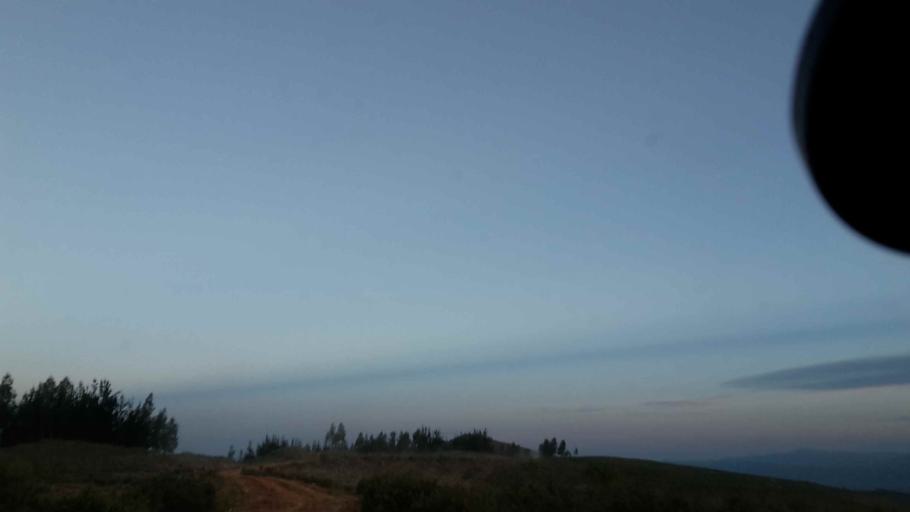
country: BO
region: Cochabamba
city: Mizque
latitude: -17.9043
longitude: -65.5139
